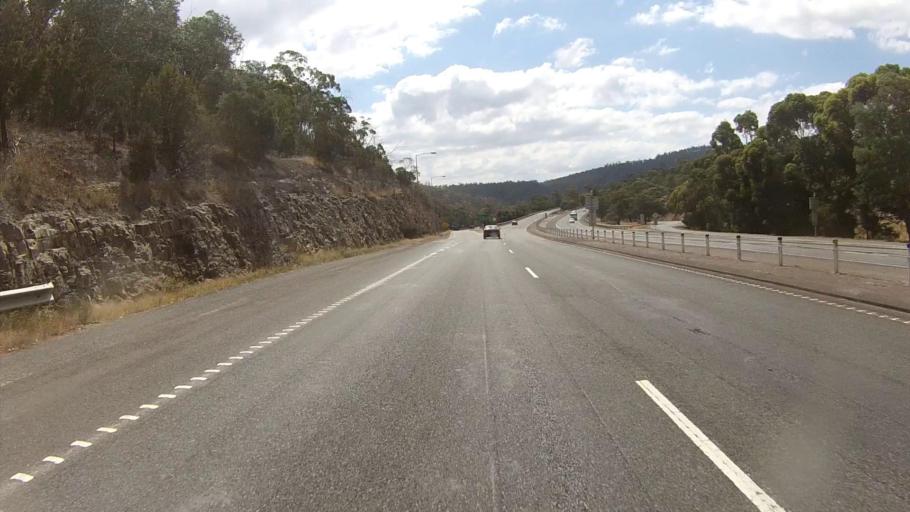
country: AU
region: Tasmania
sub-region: Clarence
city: Cambridge
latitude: -42.8481
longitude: 147.4194
